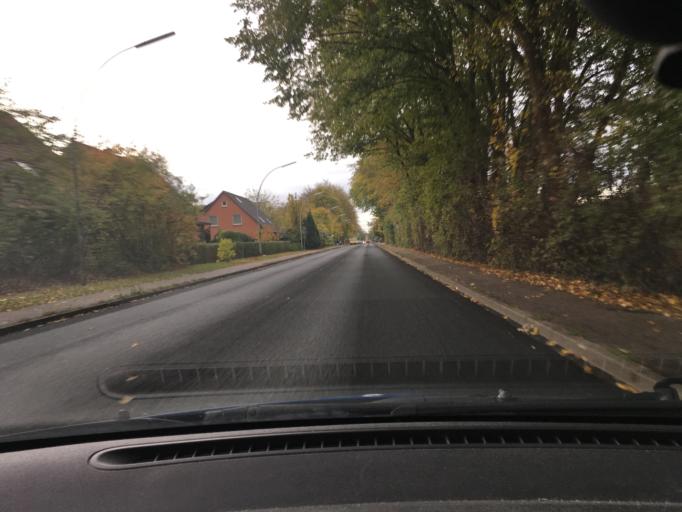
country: DE
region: Schleswig-Holstein
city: Wentorf bei Hamburg
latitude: 53.4912
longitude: 10.2657
